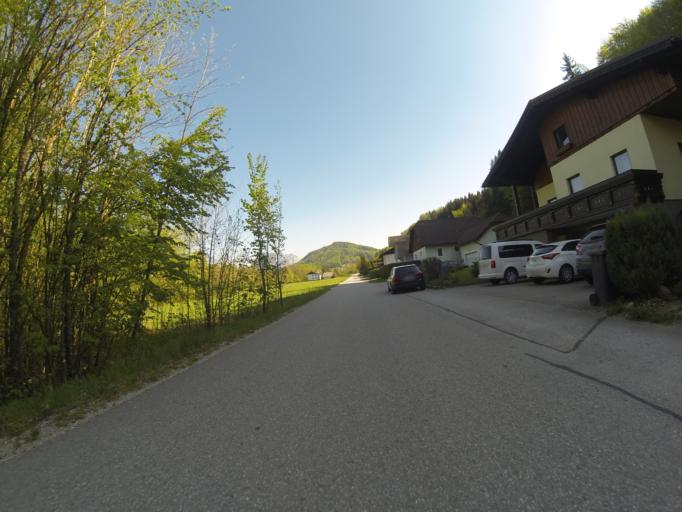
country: AT
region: Upper Austria
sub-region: Politischer Bezirk Gmunden
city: Altmunster
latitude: 47.9420
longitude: 13.7504
